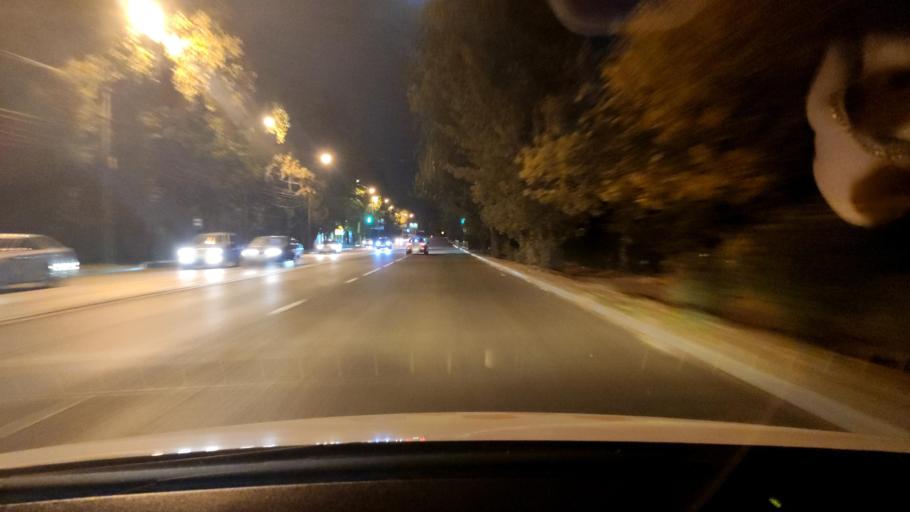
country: RU
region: Voronezj
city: Voronezh
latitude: 51.6941
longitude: 39.2010
